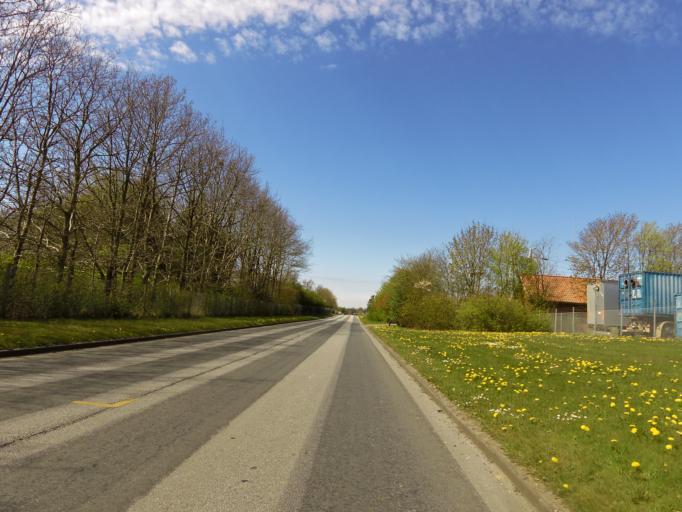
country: DK
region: South Denmark
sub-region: Tonder Kommune
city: Sherrebek
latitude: 55.1581
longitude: 8.7810
